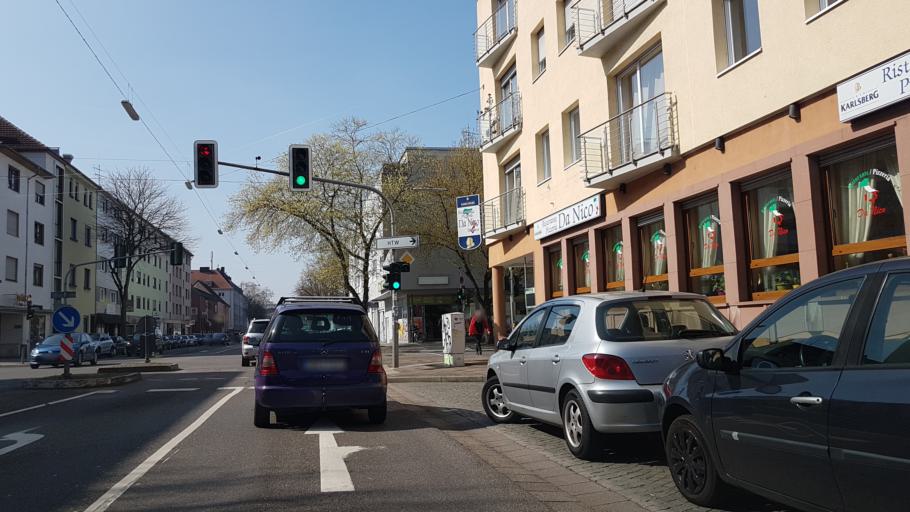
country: DE
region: Saarland
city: Saarbrucken
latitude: 49.2338
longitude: 6.9760
